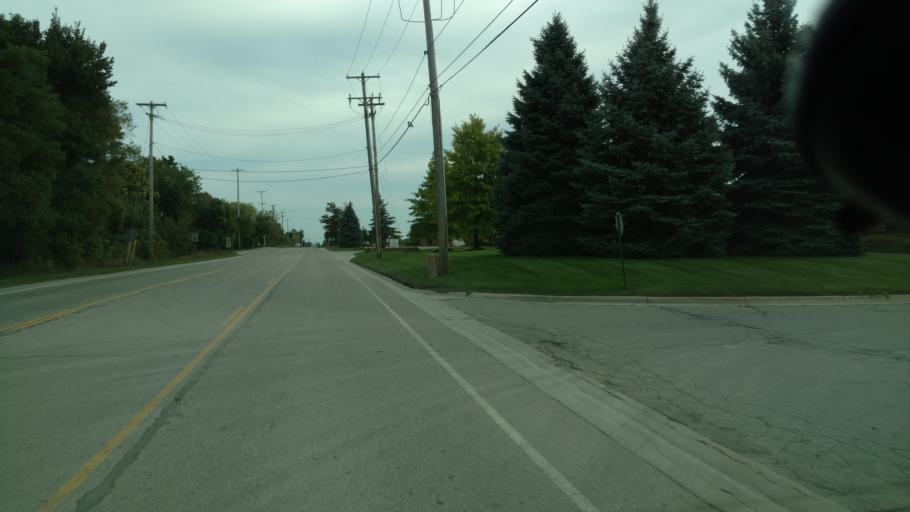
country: US
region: Michigan
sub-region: Ingham County
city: Lansing
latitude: 42.7707
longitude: -84.5231
